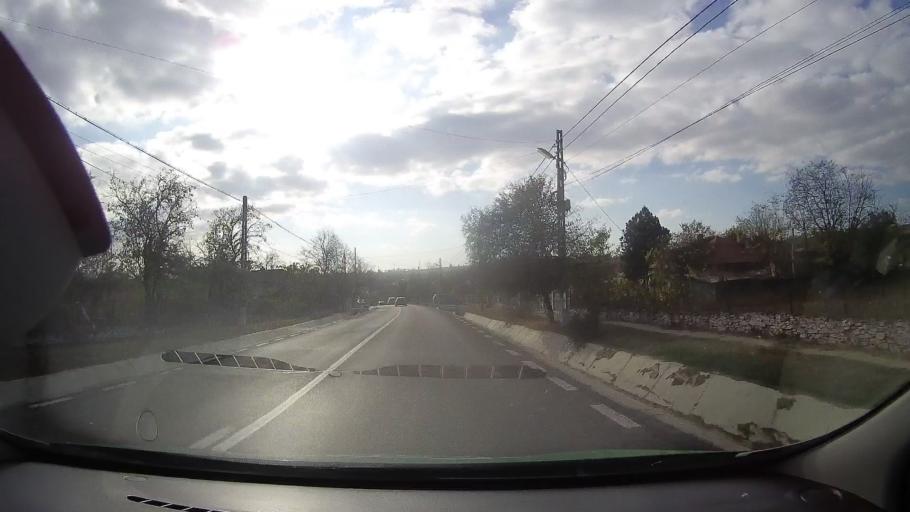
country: RO
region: Tulcea
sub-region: Comuna Topolog
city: Topolog
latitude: 44.8832
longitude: 28.3800
